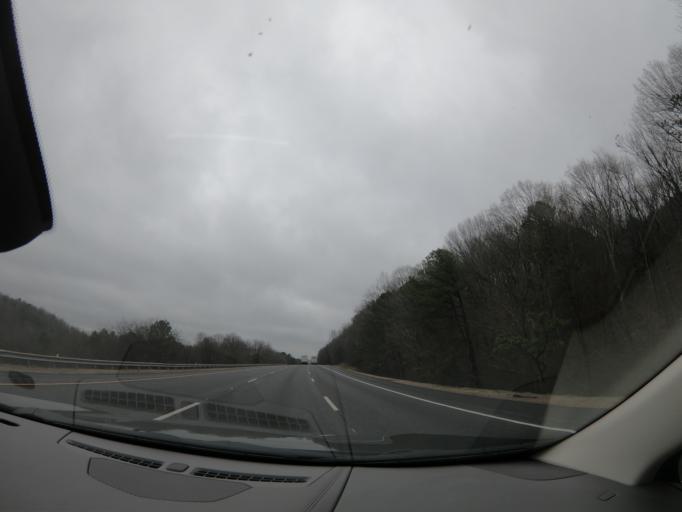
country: US
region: Georgia
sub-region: Whitfield County
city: Dalton
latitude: 34.8095
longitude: -85.0169
